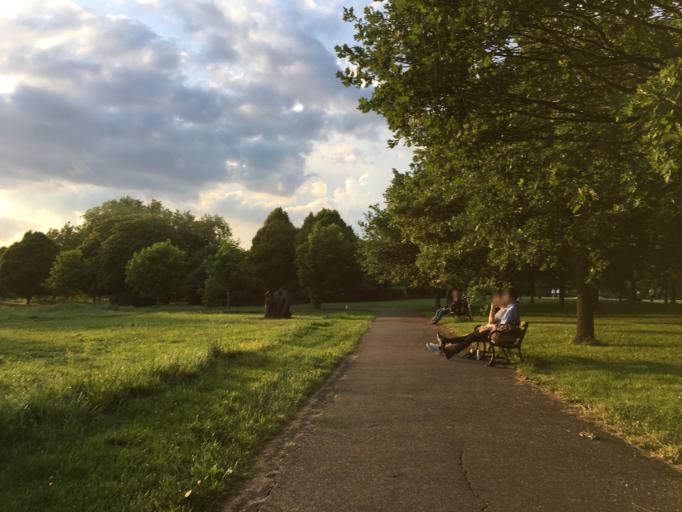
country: GB
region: England
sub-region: Greater London
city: Camden Town
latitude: 51.5319
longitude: -0.1507
